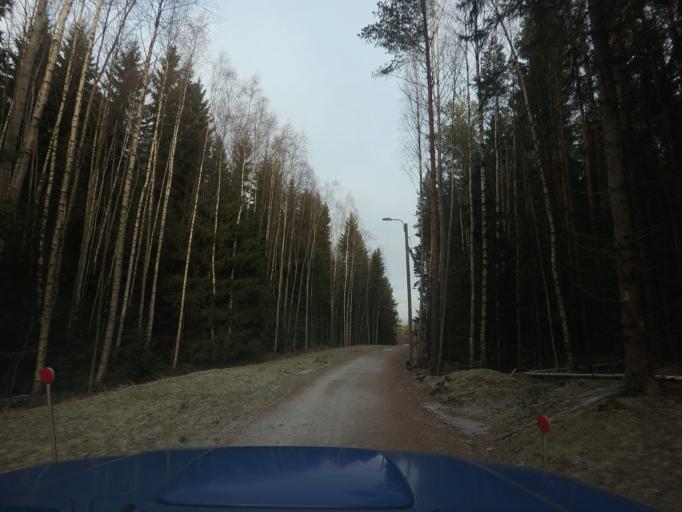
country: FI
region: Uusimaa
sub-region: Helsinki
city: Espoo
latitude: 60.1830
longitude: 24.6776
